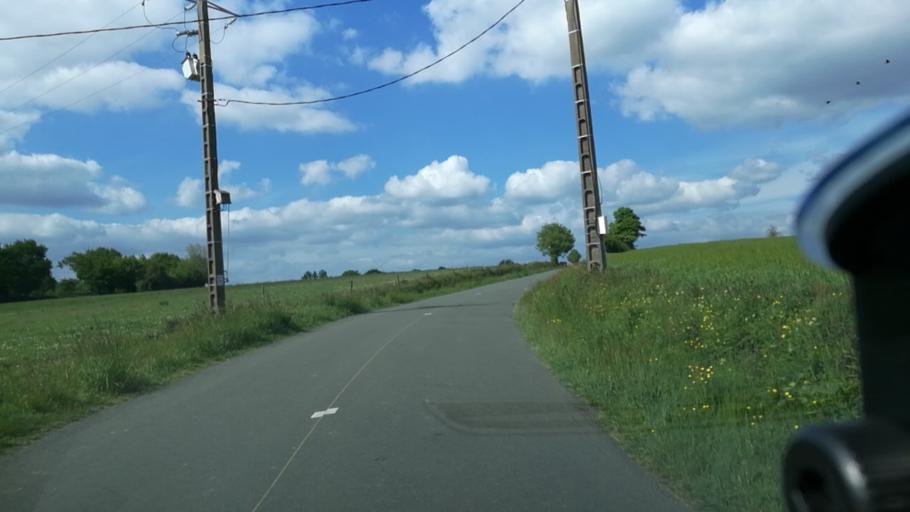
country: FR
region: Brittany
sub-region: Departement d'Ille-et-Vilaine
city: Martigne-Ferchaud
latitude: 47.8456
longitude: -1.3233
